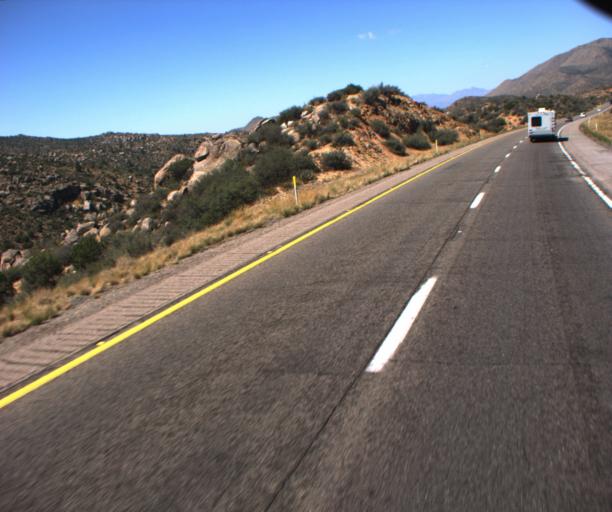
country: US
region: Arizona
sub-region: Mohave County
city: Peach Springs
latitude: 35.1790
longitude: -113.4847
